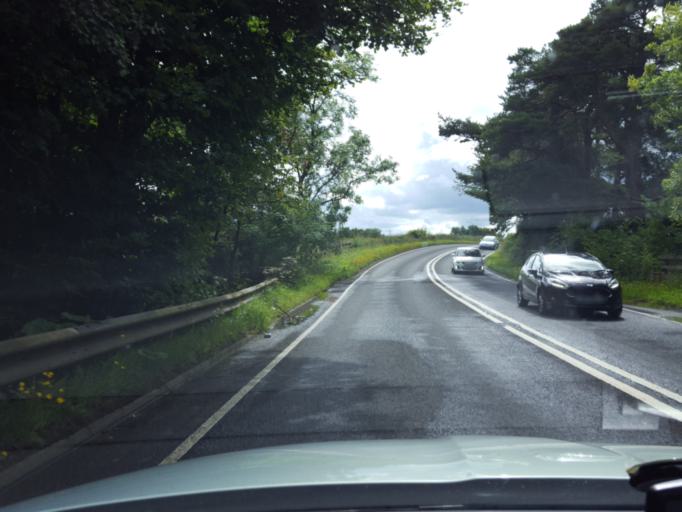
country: GB
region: Scotland
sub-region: West Lothian
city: Bathgate
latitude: 55.9360
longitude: -3.6745
